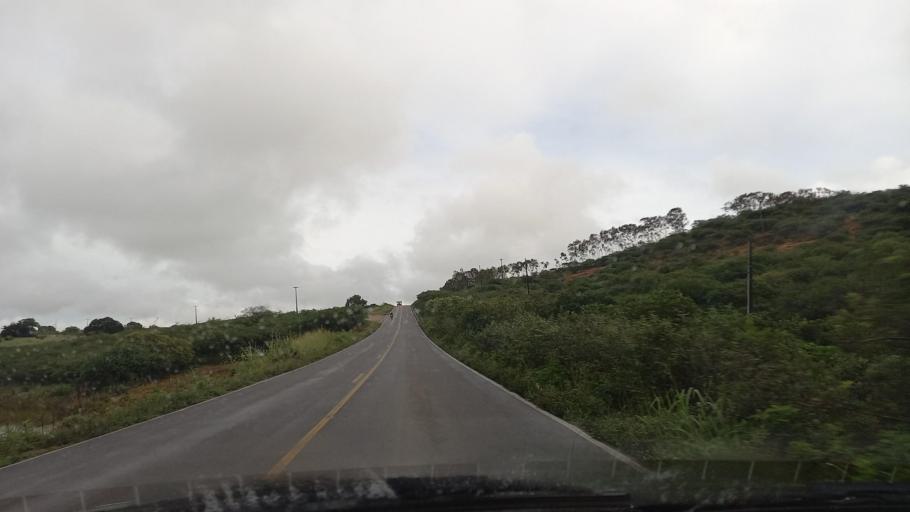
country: BR
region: Pernambuco
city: Garanhuns
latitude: -8.8429
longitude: -36.5294
